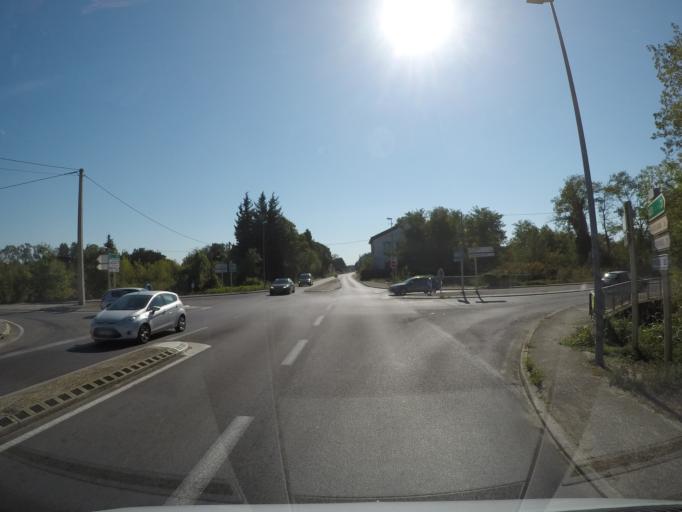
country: FR
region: Languedoc-Roussillon
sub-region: Departement du Gard
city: Moussac
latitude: 43.9779
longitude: 4.2087
